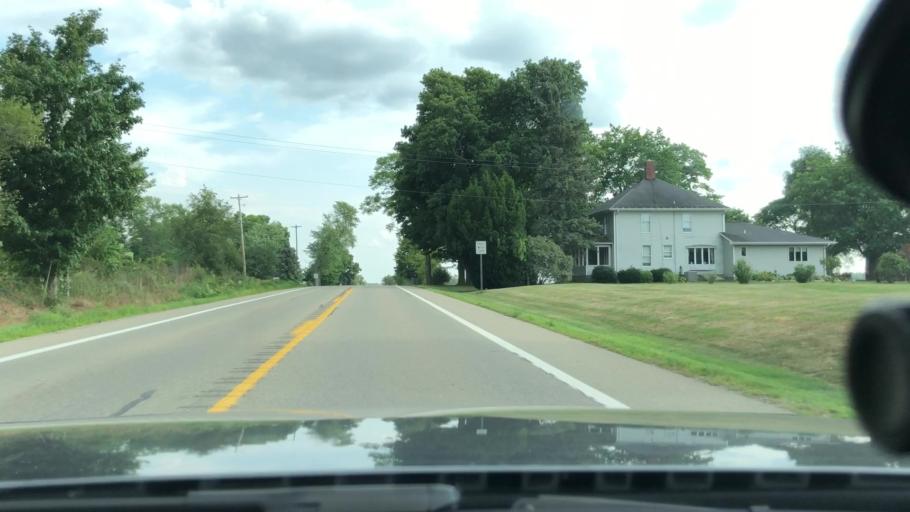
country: US
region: Michigan
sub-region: Washtenaw County
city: Chelsea
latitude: 42.2827
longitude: -84.0311
